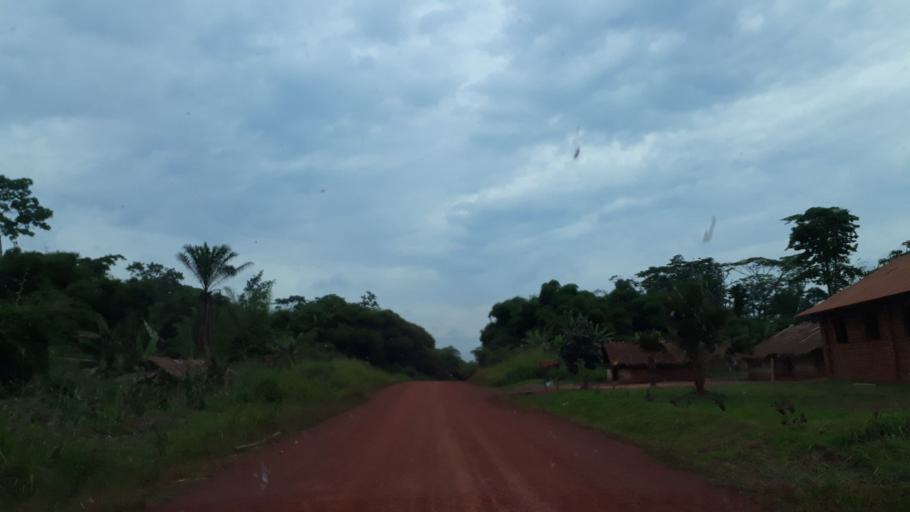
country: CD
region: Eastern Province
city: Kisangani
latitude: 0.6211
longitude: 26.0310
